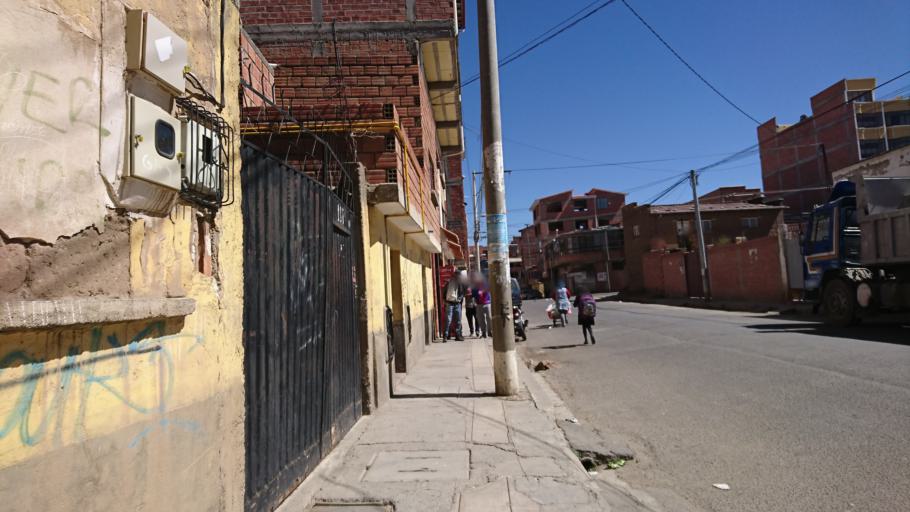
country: BO
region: La Paz
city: La Paz
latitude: -16.5008
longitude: -68.1034
